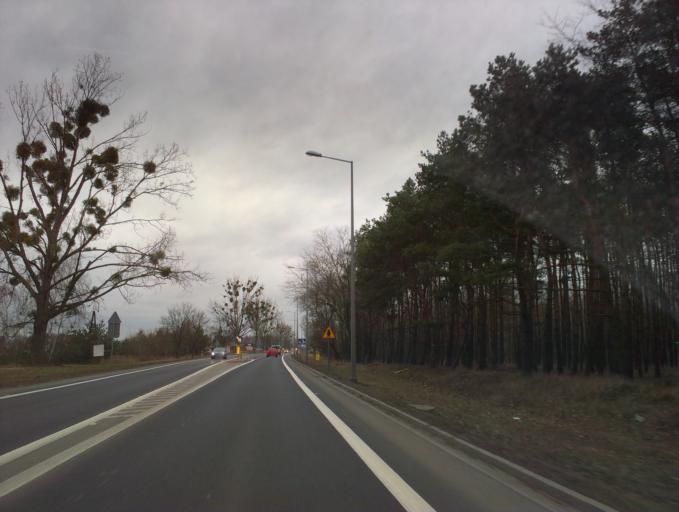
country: PL
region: Greater Poland Voivodeship
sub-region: Powiat poznanski
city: Zlotniki
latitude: 52.5336
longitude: 16.8351
